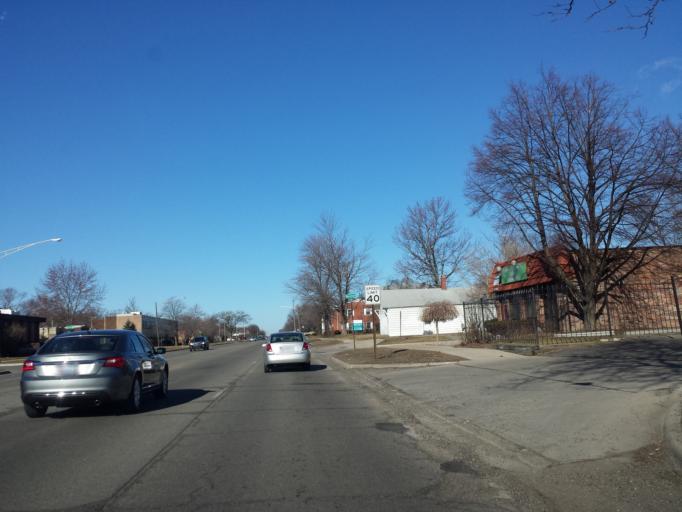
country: US
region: Michigan
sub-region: Oakland County
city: Lathrup Village
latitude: 42.5029
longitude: -83.2047
